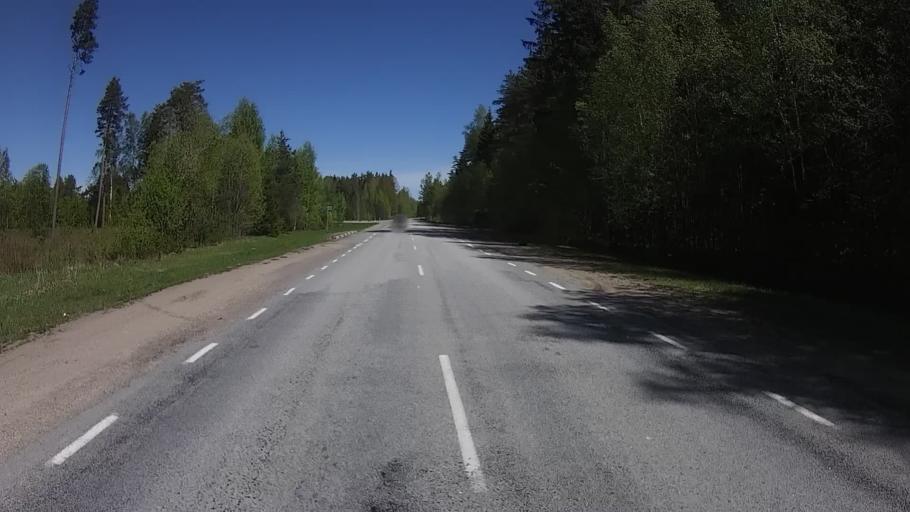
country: EE
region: Polvamaa
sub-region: Raepina vald
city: Rapina
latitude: 58.0658
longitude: 27.3988
